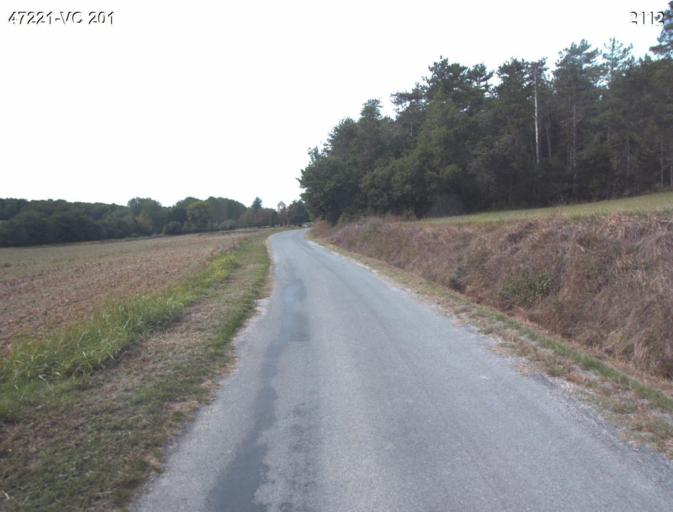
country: FR
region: Aquitaine
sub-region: Departement du Lot-et-Garonne
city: Mezin
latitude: 44.1102
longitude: 0.2444
